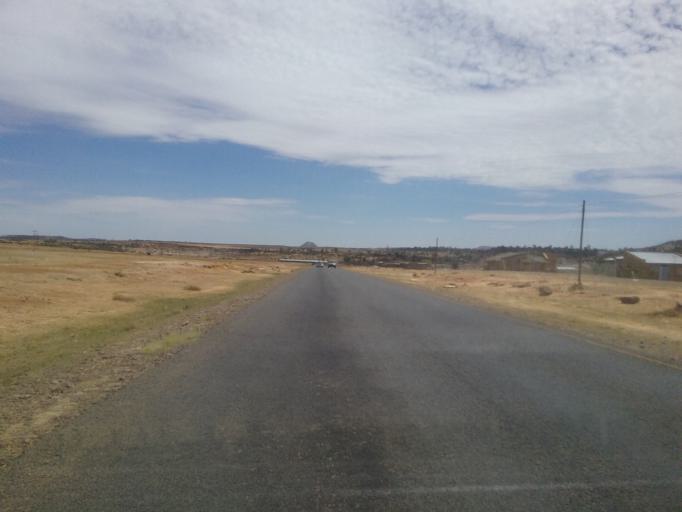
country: LS
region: Mafeteng
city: Mafeteng
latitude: -29.8551
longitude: 27.2328
